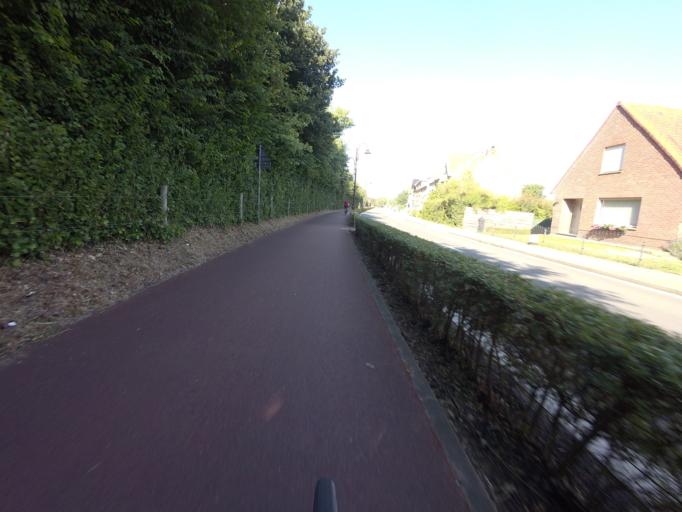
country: BE
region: Flanders
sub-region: Provincie West-Vlaanderen
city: De Haan
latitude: 51.2638
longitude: 3.0088
